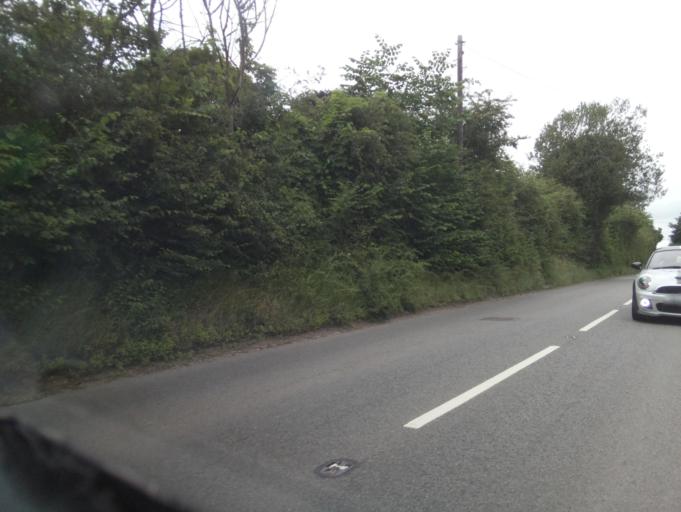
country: GB
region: England
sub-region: Nottinghamshire
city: East Leake
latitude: 52.8135
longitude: -1.1407
